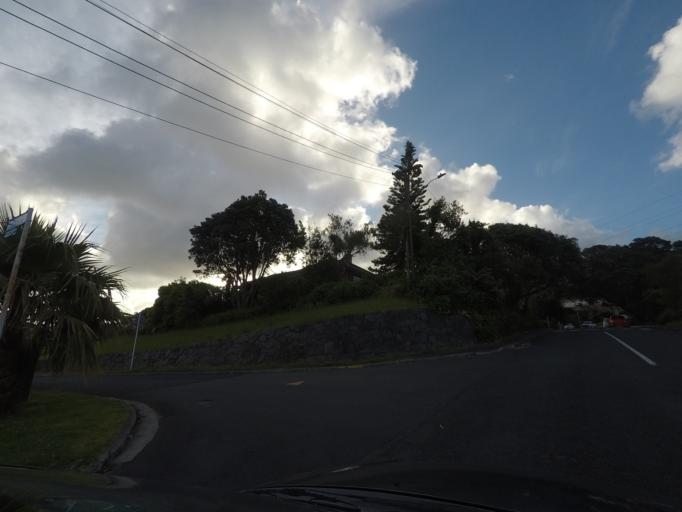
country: NZ
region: Auckland
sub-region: Auckland
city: Mangere
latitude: -36.9260
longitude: 174.7597
